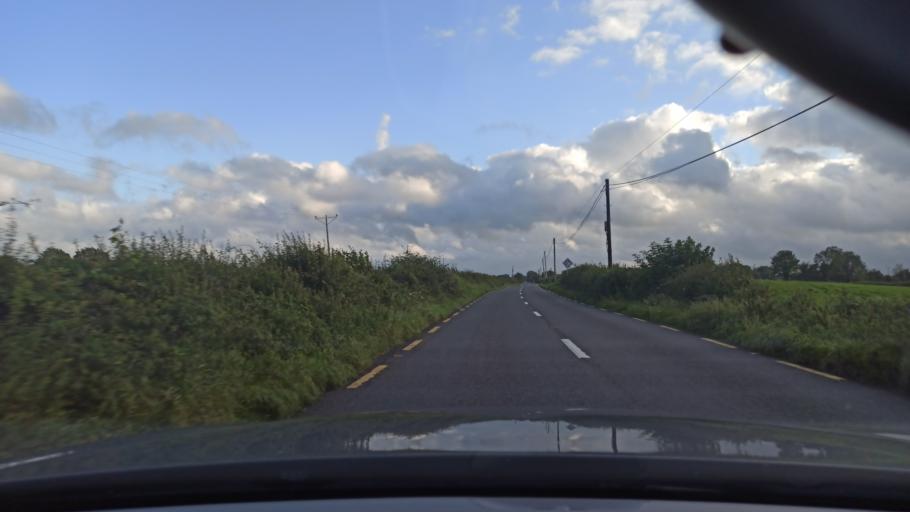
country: IE
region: Munster
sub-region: North Tipperary
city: Templemore
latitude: 52.8613
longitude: -7.8132
